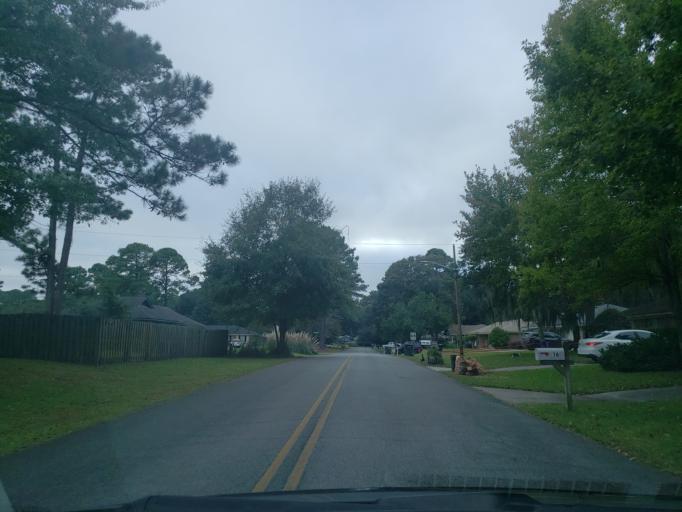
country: US
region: Georgia
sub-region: Chatham County
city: Montgomery
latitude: 31.9534
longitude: -81.1090
